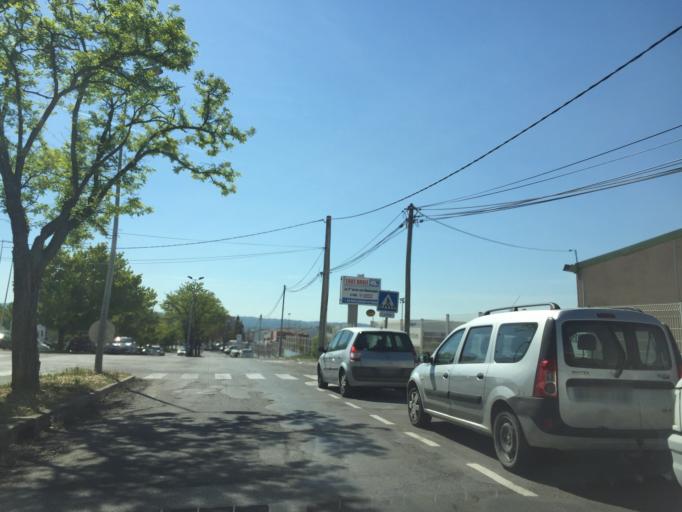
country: FR
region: Provence-Alpes-Cote d'Azur
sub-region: Departement des Alpes-de-Haute-Provence
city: Manosque
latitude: 43.8221
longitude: 5.7969
